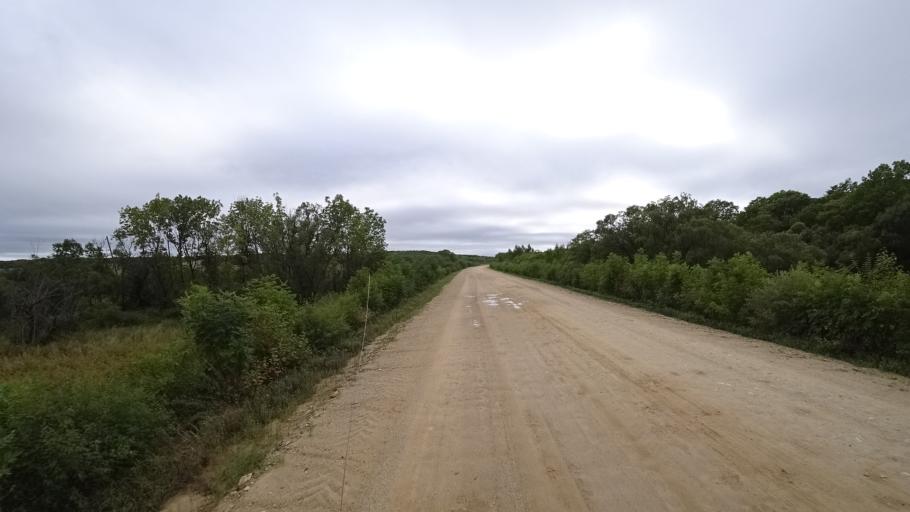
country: RU
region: Primorskiy
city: Rettikhovka
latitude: 44.1237
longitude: 132.6376
